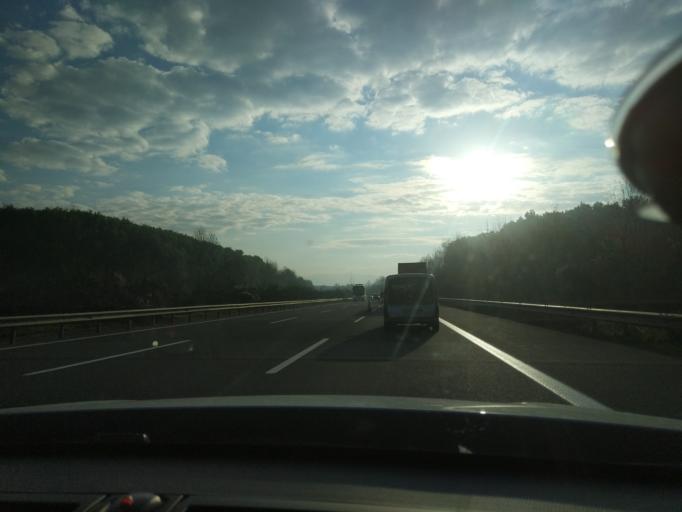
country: TR
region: Duzce
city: Duzce
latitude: 40.8108
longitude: 31.1213
